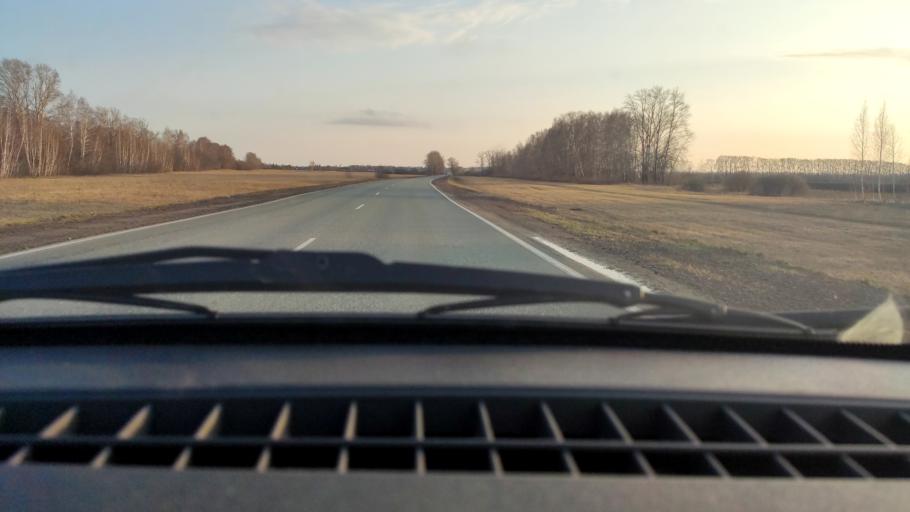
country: RU
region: Bashkortostan
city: Chishmy
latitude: 54.4103
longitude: 55.2219
